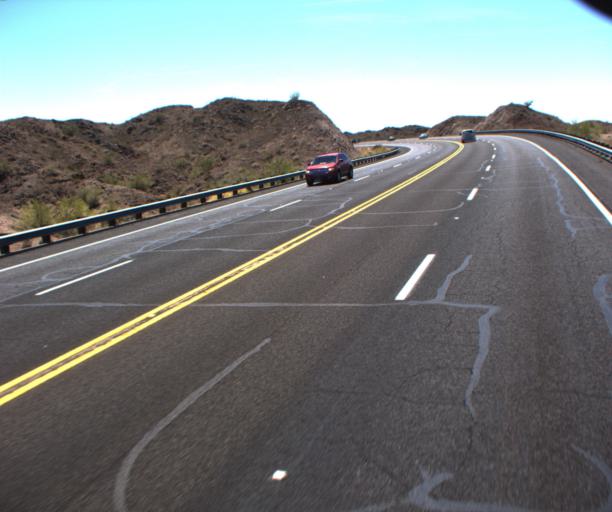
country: US
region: Arizona
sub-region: La Paz County
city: Cienega Springs
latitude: 34.2010
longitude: -114.2089
